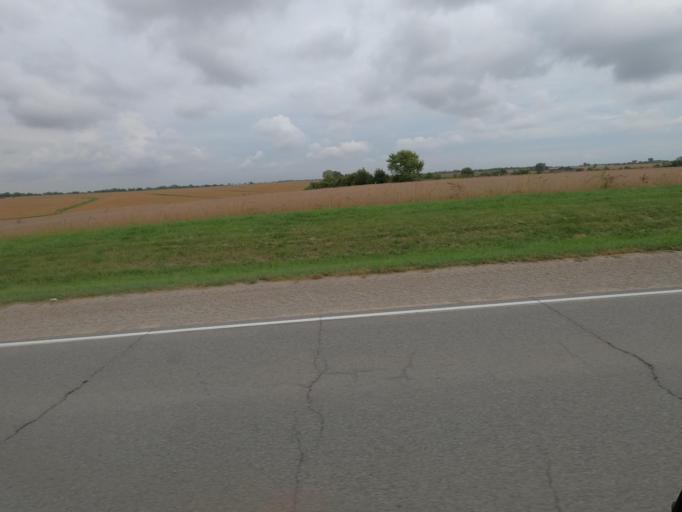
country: US
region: Iowa
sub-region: Wapello County
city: Ottumwa
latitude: 40.9610
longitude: -92.2365
